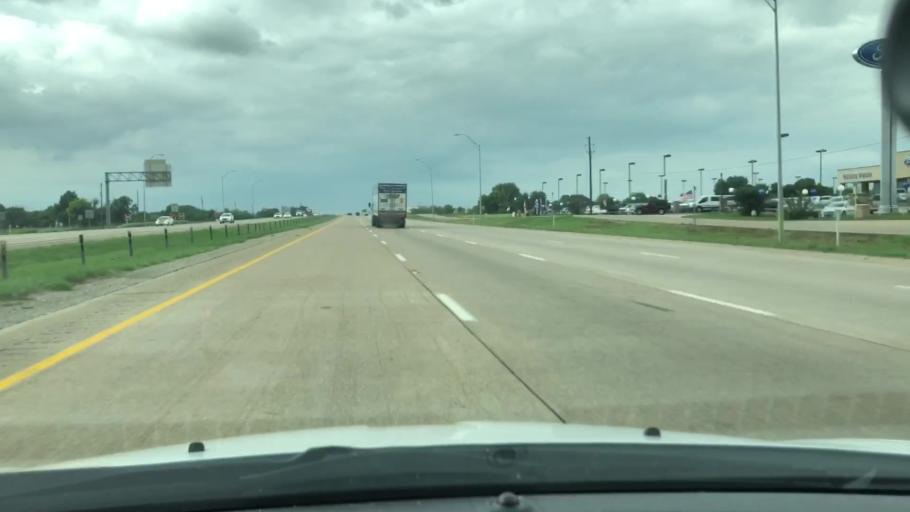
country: US
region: Texas
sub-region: Ellis County
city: Ennis
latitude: 32.3395
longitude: -96.6190
